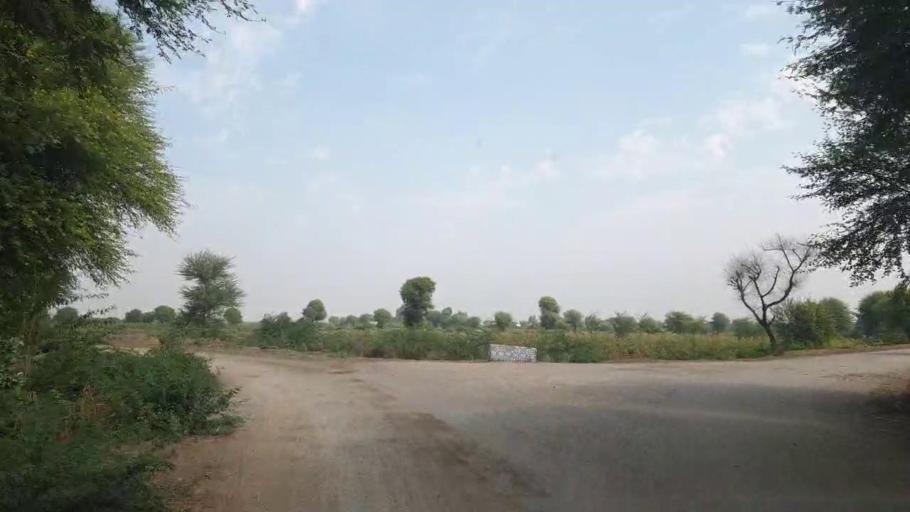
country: PK
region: Sindh
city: Rajo Khanani
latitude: 24.9686
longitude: 68.9966
